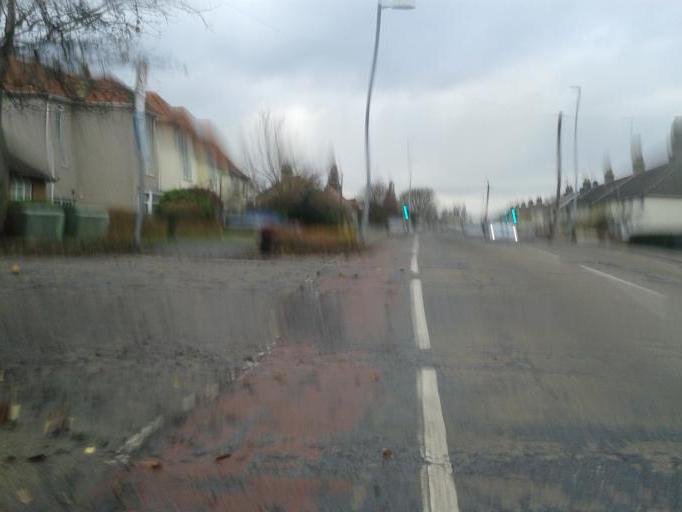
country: GB
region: England
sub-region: Cambridgeshire
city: Cambridge
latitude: 52.2027
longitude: 0.1533
